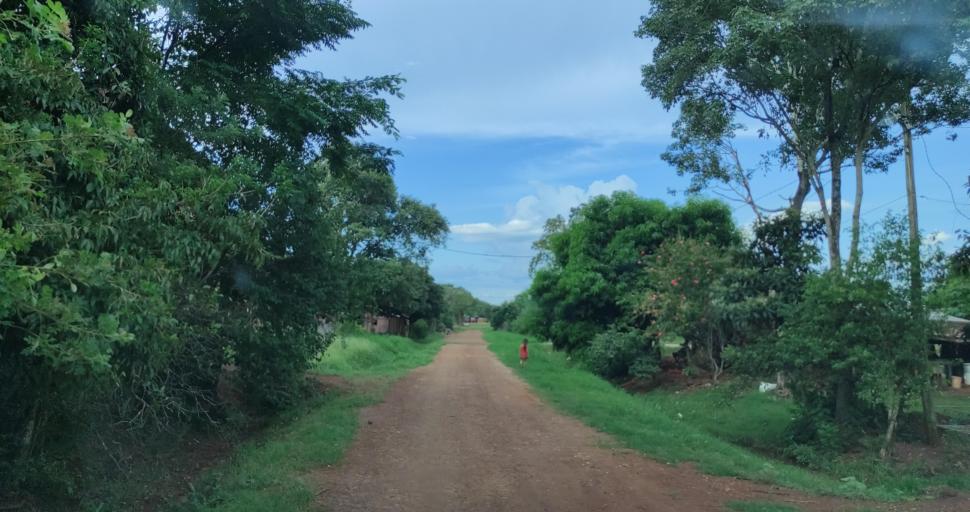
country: AR
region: Misiones
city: Gobernador Roca
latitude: -27.1871
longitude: -55.4683
